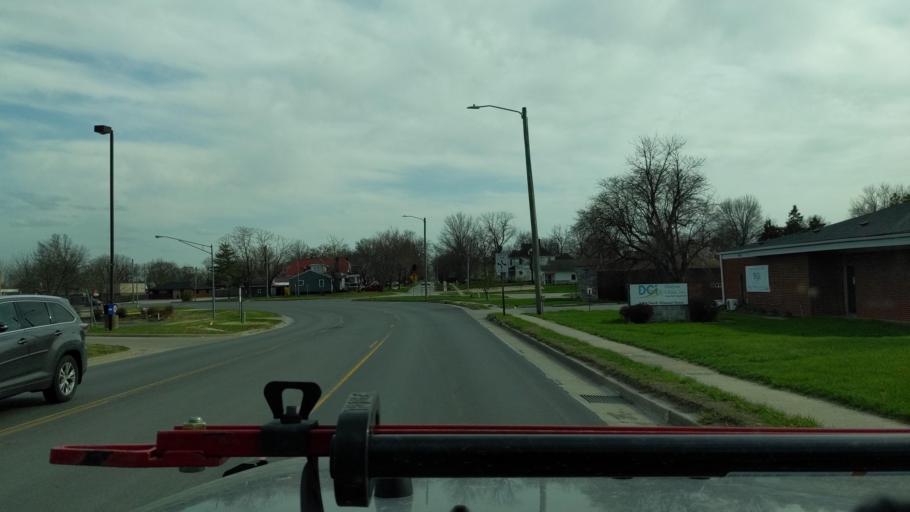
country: US
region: Missouri
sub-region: Macon County
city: Macon
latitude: 39.7479
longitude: -92.4681
